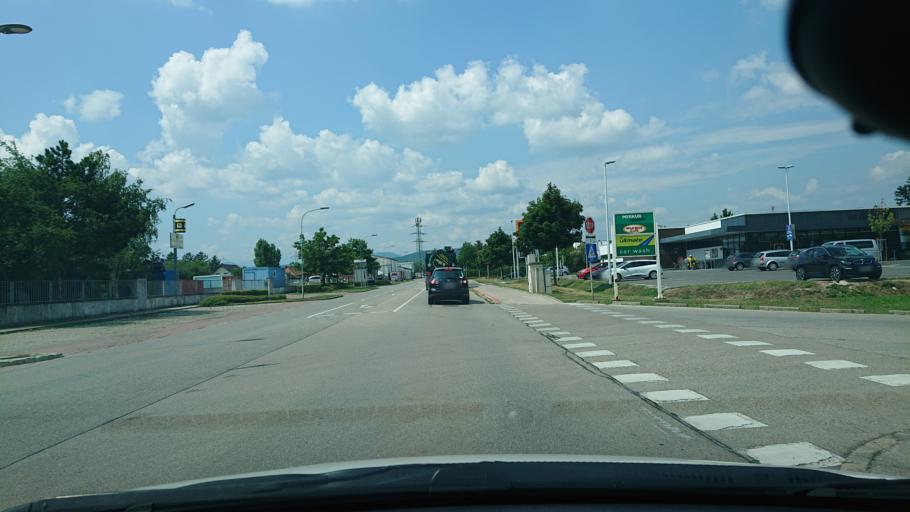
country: AT
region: Lower Austria
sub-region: Politischer Bezirk Baden
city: Leobersdorf
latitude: 47.9343
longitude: 16.2167
